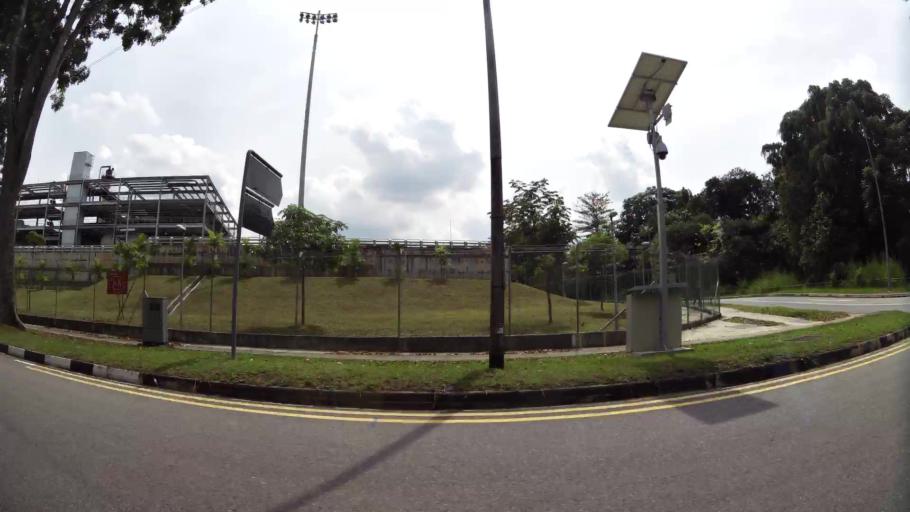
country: MY
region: Johor
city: Johor Bahru
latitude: 1.4106
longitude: 103.7627
